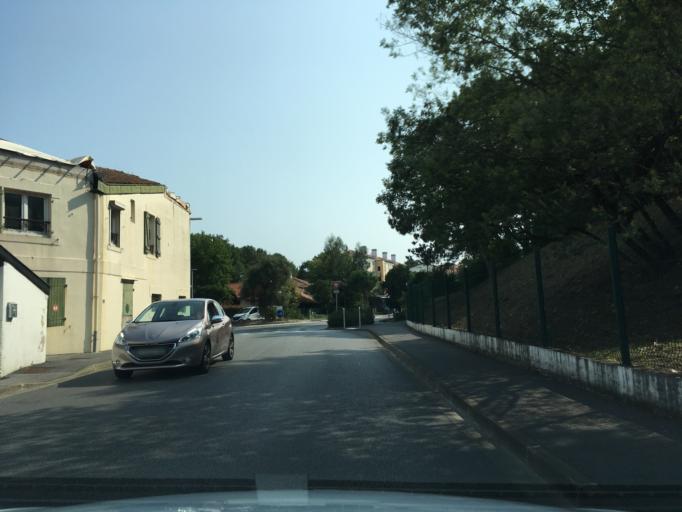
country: FR
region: Aquitaine
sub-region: Departement des Pyrenees-Atlantiques
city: Bayonne
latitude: 43.5076
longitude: -1.5024
